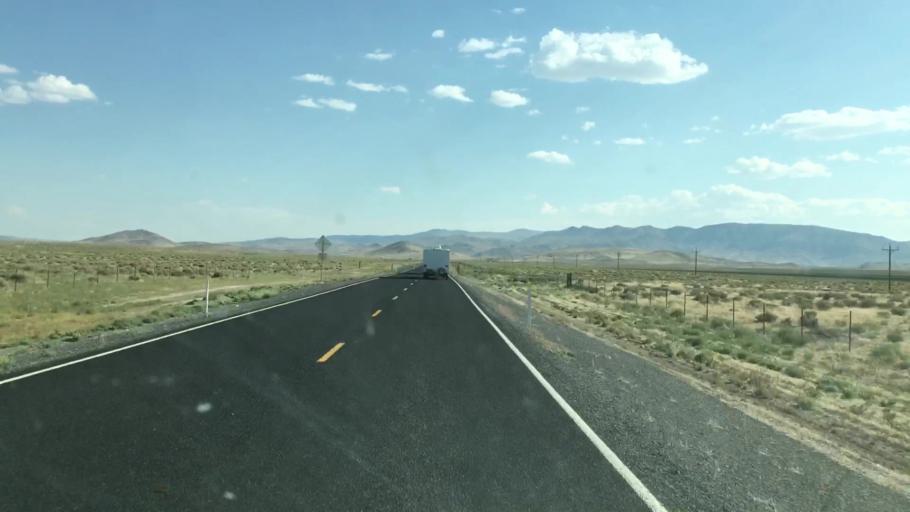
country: US
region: Nevada
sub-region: Lyon County
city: Fernley
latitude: 39.6702
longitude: -119.3321
